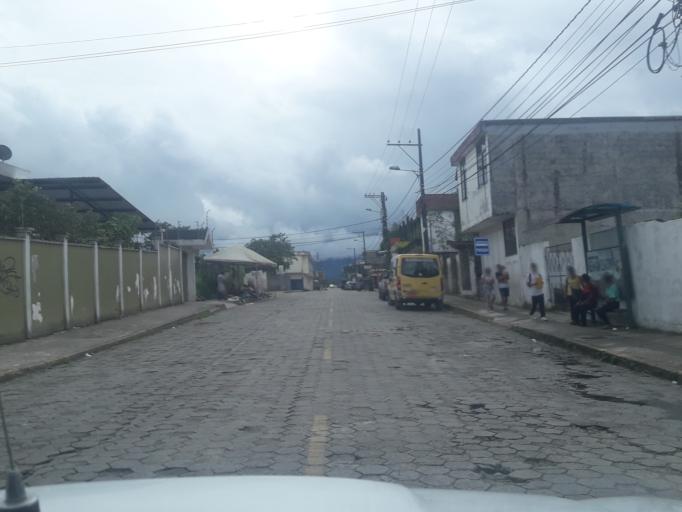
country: EC
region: Napo
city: Tena
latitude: -0.9883
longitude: -77.8162
